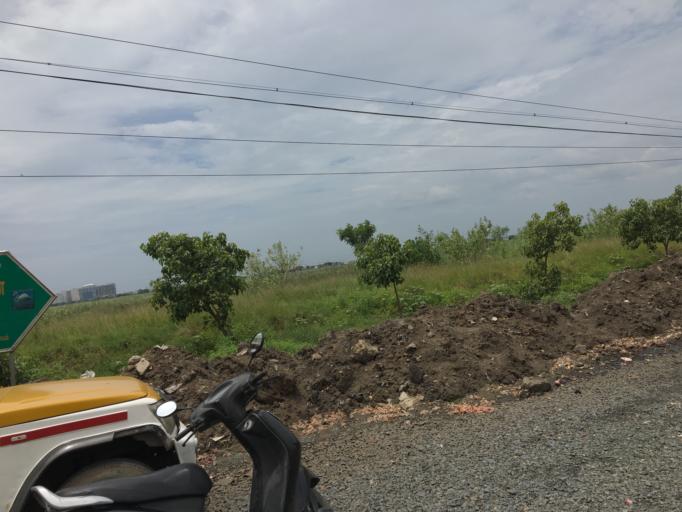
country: IN
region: Tamil Nadu
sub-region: Kancheepuram
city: Madipakkam
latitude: 12.9548
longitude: 80.2126
